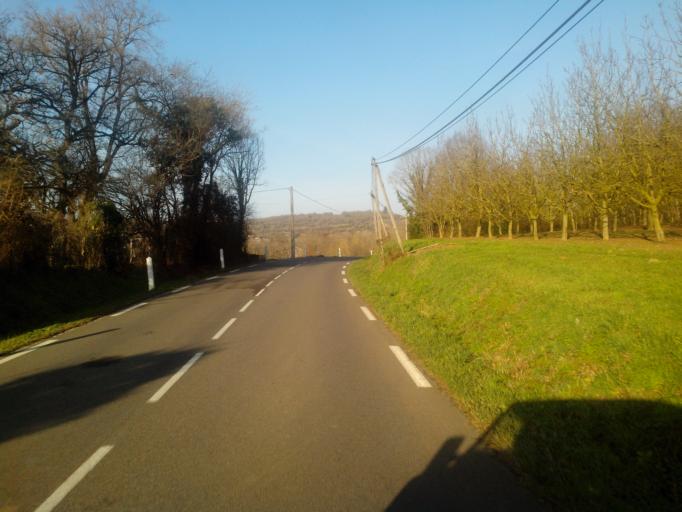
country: FR
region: Midi-Pyrenees
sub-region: Departement du Lot
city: Vayrac
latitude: 44.9014
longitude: 1.6229
